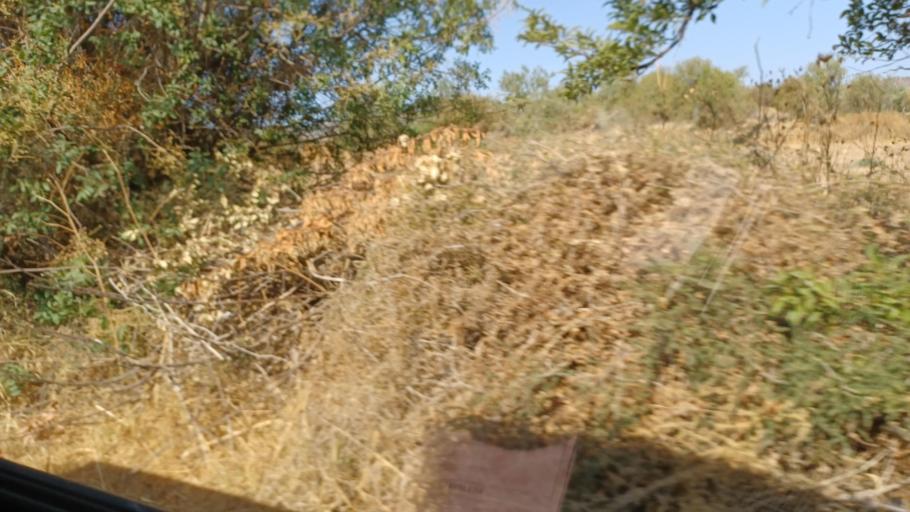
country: CY
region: Pafos
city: Tala
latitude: 34.9127
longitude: 32.4824
